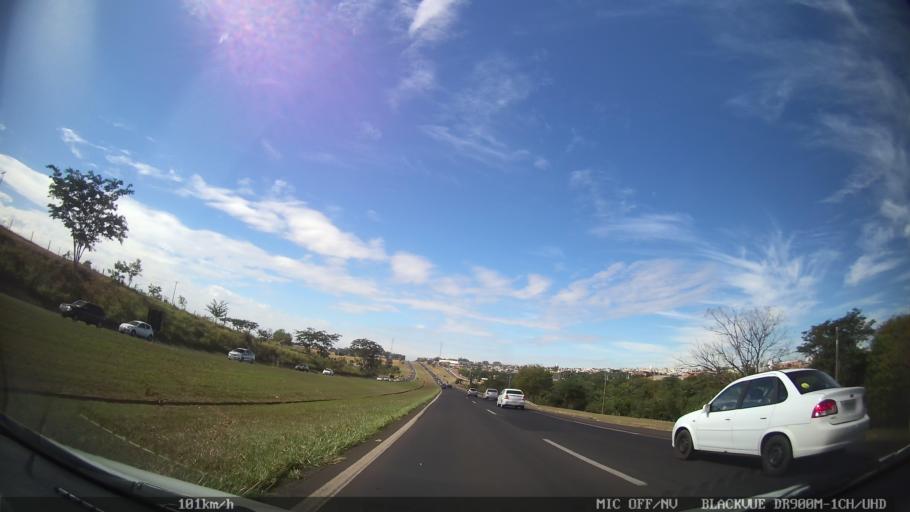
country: BR
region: Sao Paulo
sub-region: Sao Jose Do Rio Preto
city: Sao Jose do Rio Preto
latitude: -20.8144
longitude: -49.4721
